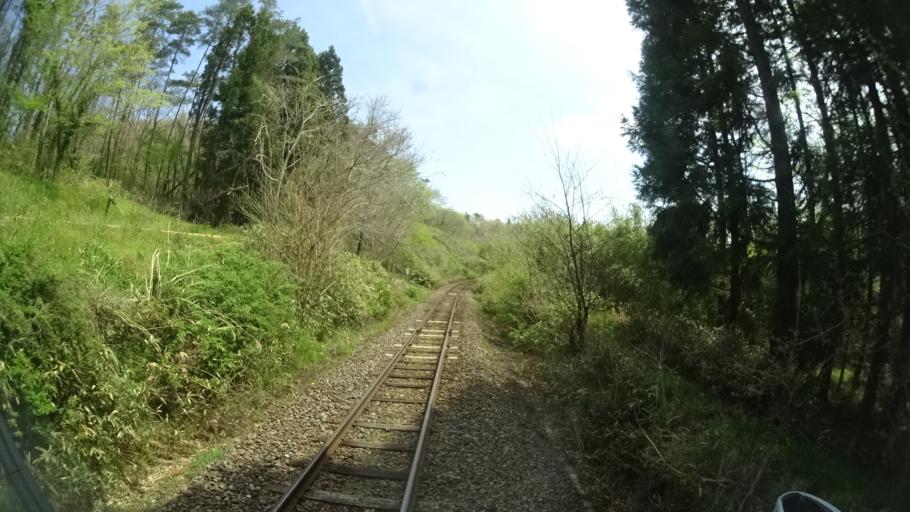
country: JP
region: Iwate
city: Ichinoseki
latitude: 38.9939
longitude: 141.2849
